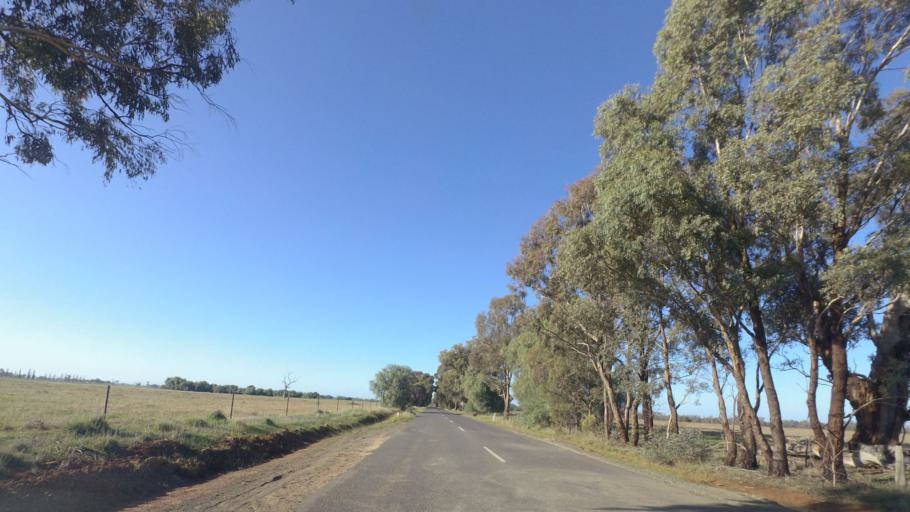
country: AU
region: Victoria
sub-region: Greater Bendigo
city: Epsom
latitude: -36.6495
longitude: 144.5245
